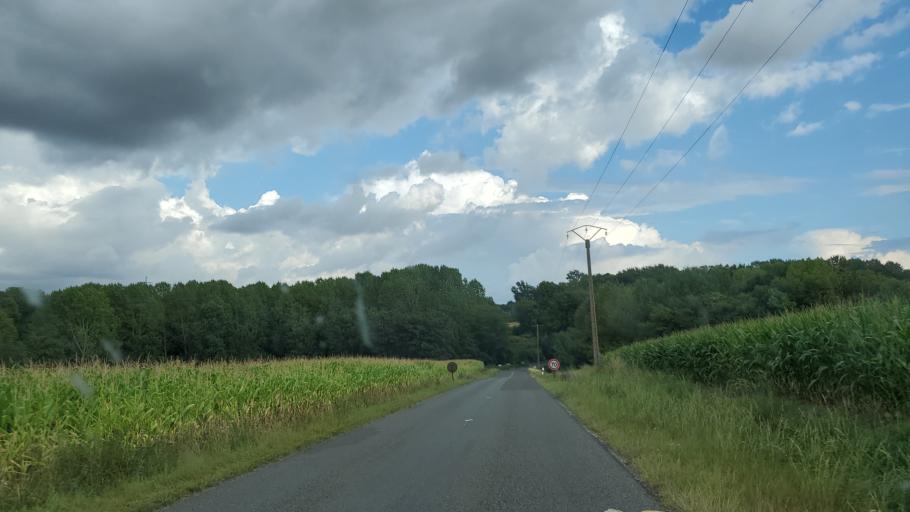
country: FR
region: Ile-de-France
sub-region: Departement de Seine-et-Marne
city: Chailly-en-Brie
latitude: 48.7799
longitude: 3.1683
